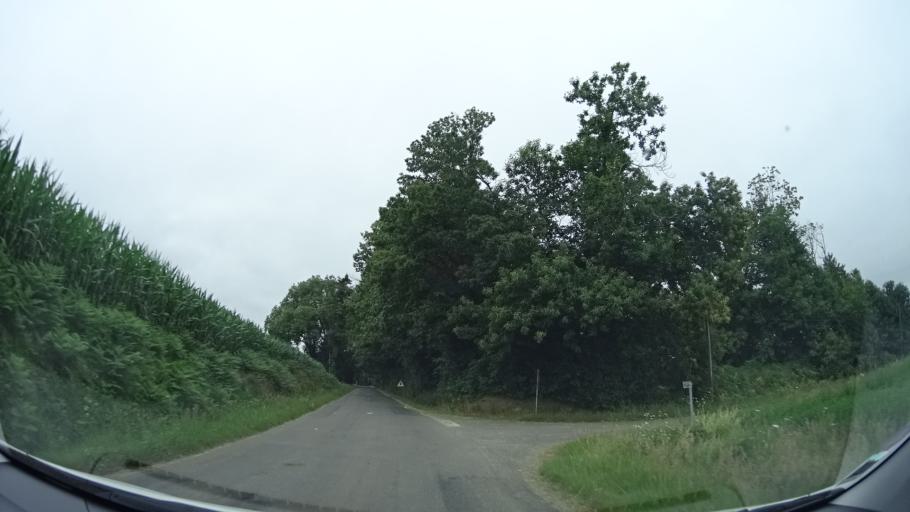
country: FR
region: Brittany
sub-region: Departement d'Ille-et-Vilaine
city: Saint-Domineuc
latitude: 48.3260
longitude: -1.9312
